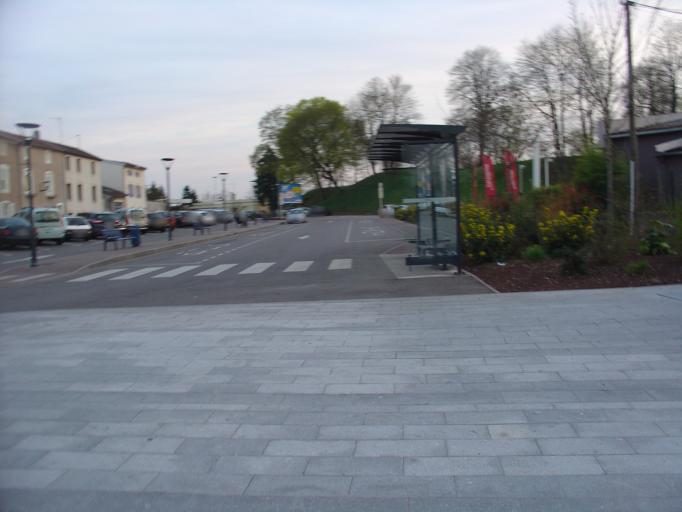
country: FR
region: Lorraine
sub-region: Departement de Meurthe-et-Moselle
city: Toul
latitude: 48.6742
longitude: 5.8861
